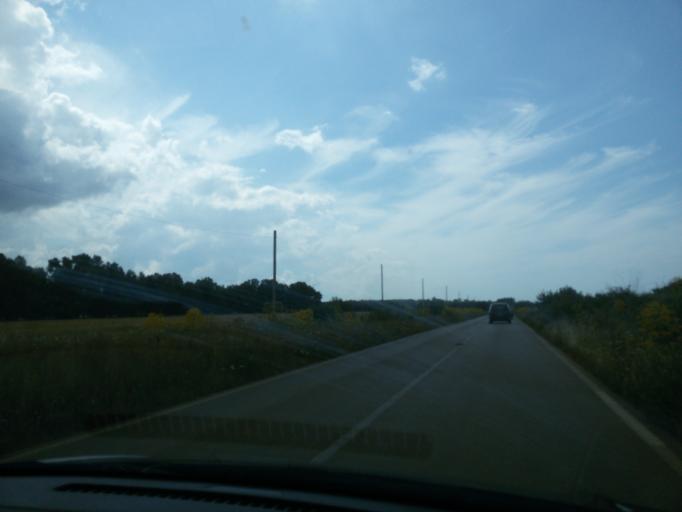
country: IT
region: Apulia
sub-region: Provincia di Brindisi
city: San Pancrazio Salentino
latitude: 40.3351
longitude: 17.8506
